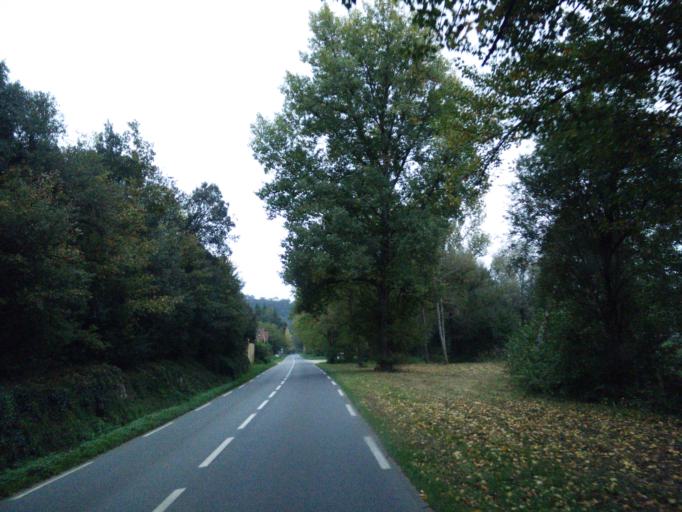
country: FR
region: Aquitaine
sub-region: Departement de la Dordogne
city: Carsac-Aillac
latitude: 44.8050
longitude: 1.2984
